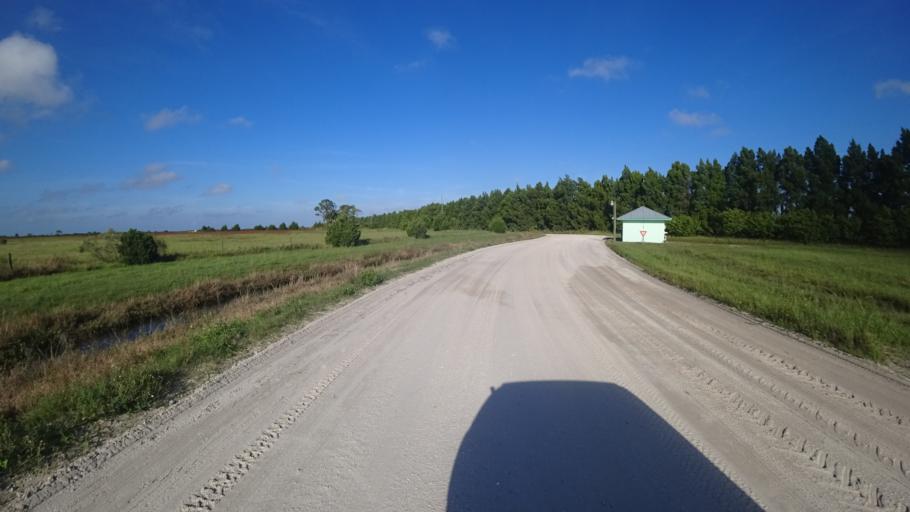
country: US
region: Florida
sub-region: Hillsborough County
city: Wimauma
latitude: 27.5418
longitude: -82.3362
